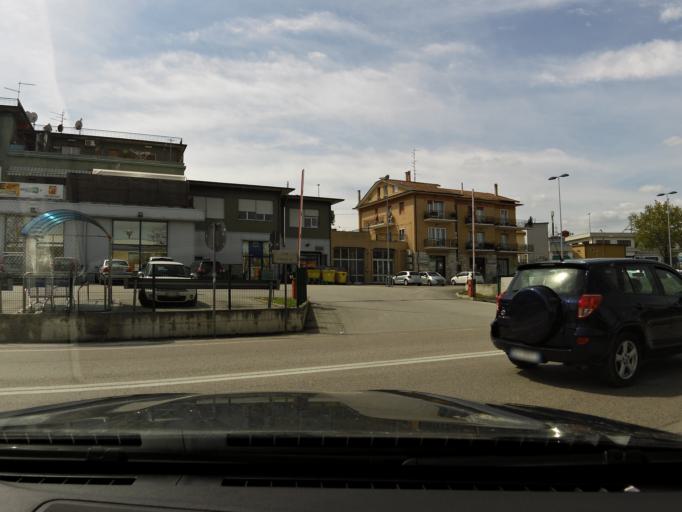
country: IT
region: The Marches
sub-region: Provincia di Ancona
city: Ancona
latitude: 43.5697
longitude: 13.5096
